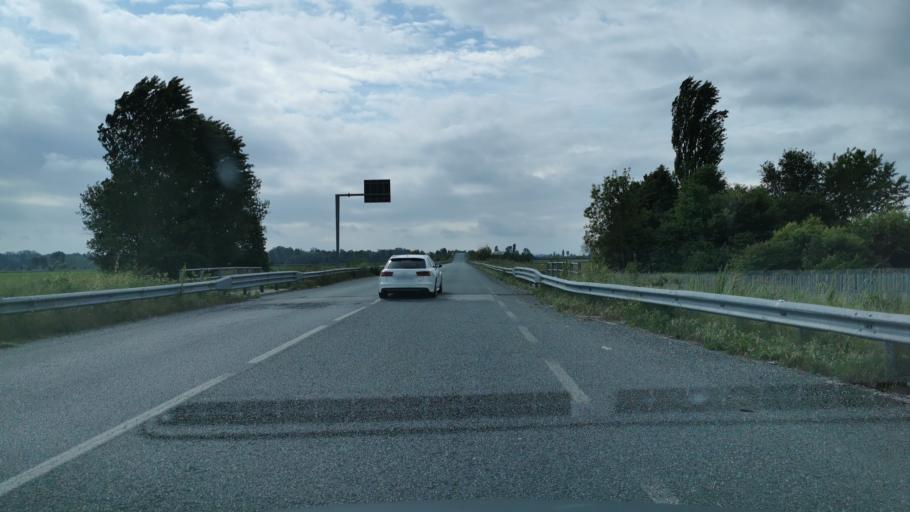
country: IT
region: Piedmont
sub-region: Provincia di Cuneo
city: Racconigi
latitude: 44.7998
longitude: 7.6932
